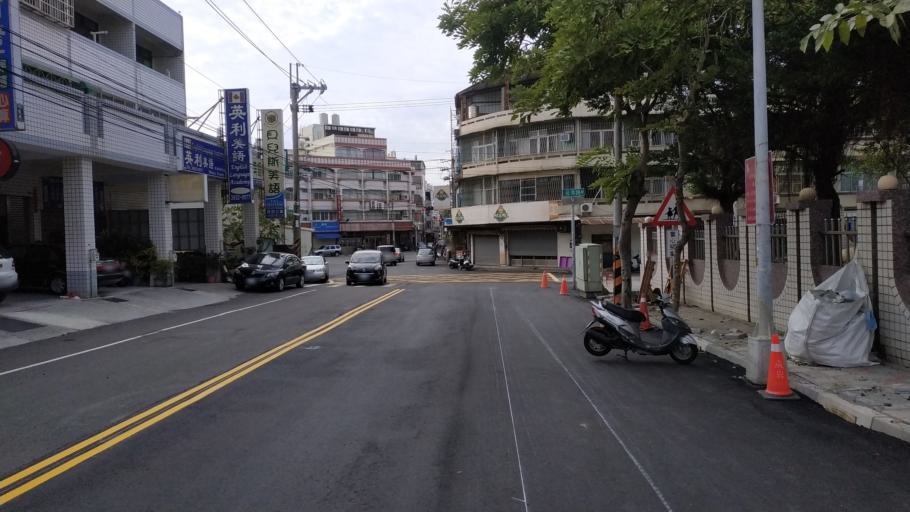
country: TW
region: Taiwan
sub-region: Taichung City
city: Taichung
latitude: 24.2163
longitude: 120.5716
